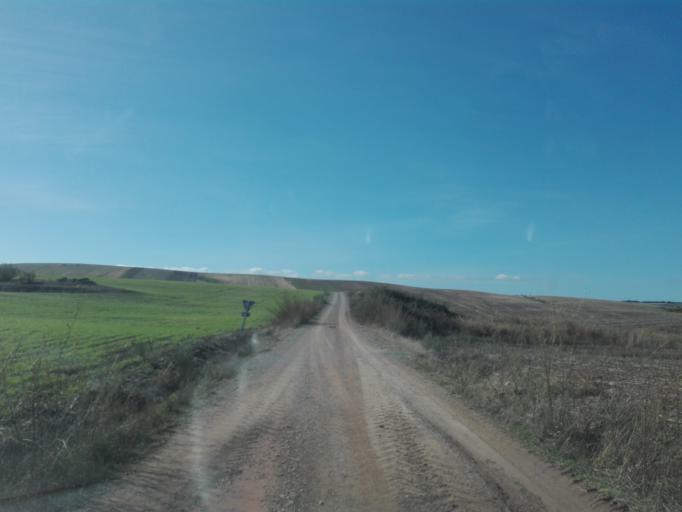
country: ES
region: Extremadura
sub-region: Provincia de Badajoz
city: Maguilla
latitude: 38.3343
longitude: -5.8943
